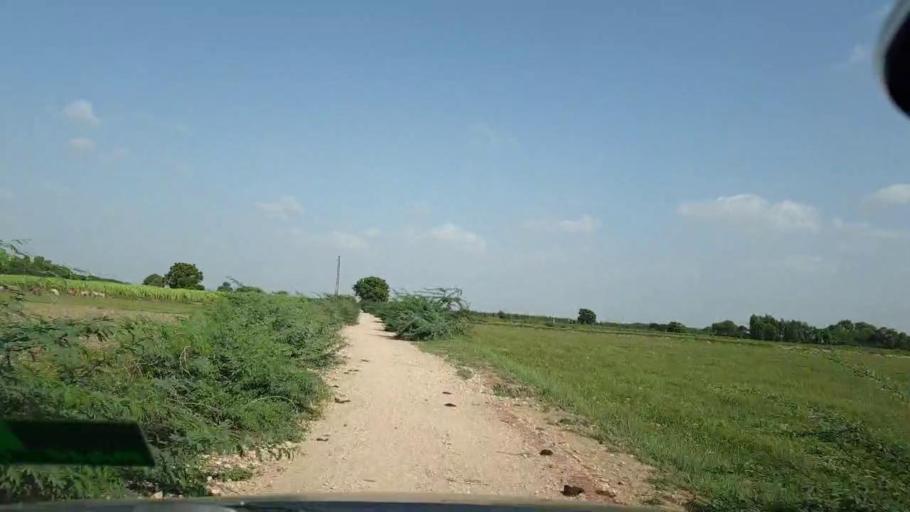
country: PK
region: Sindh
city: Tando Bago
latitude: 24.6827
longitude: 69.2022
